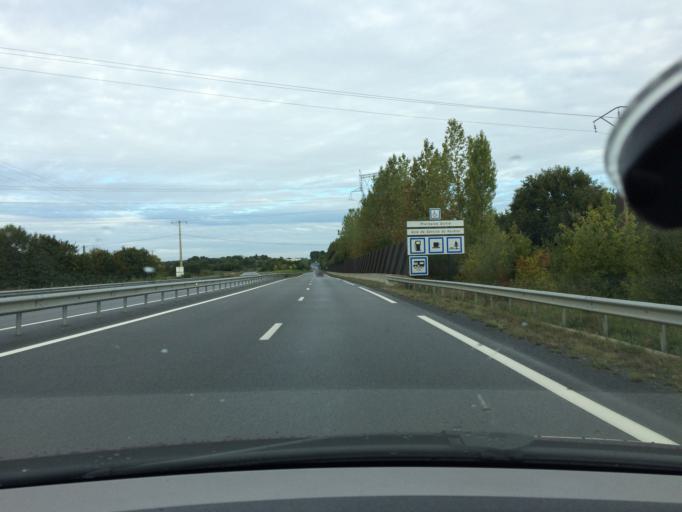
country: FR
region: Brittany
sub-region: Departement d'Ille-et-Vilaine
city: Janze
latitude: 47.9624
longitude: -1.5220
